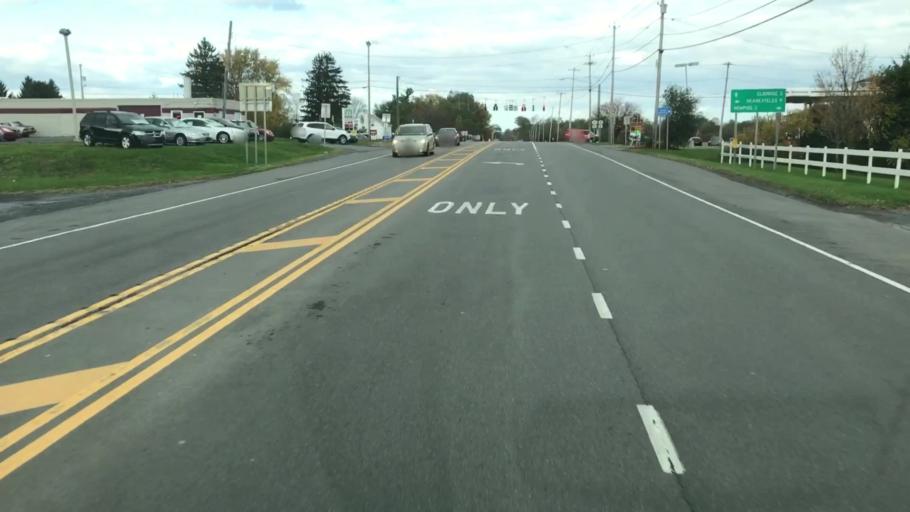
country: US
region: New York
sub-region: Onondaga County
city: Marcellus
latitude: 43.0347
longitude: -76.3635
